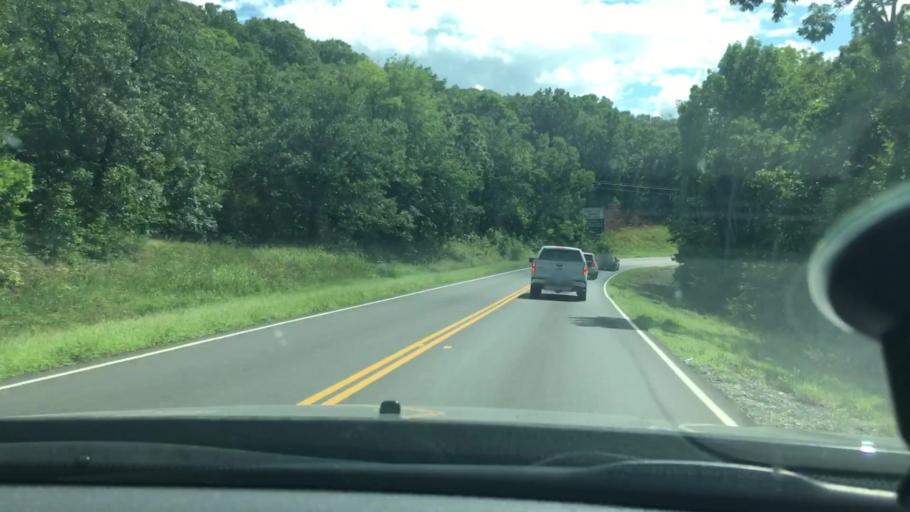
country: US
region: Oklahoma
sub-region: Sequoyah County
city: Vian
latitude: 35.6503
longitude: -94.9540
